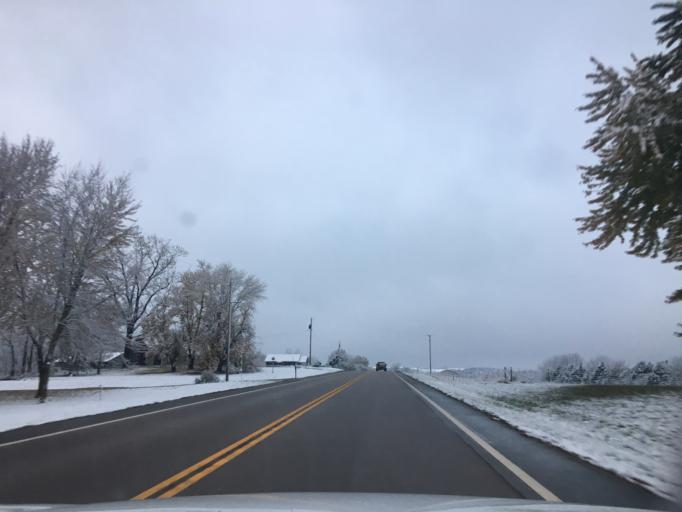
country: US
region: Missouri
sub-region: Osage County
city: Linn
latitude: 38.4742
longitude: -91.7941
